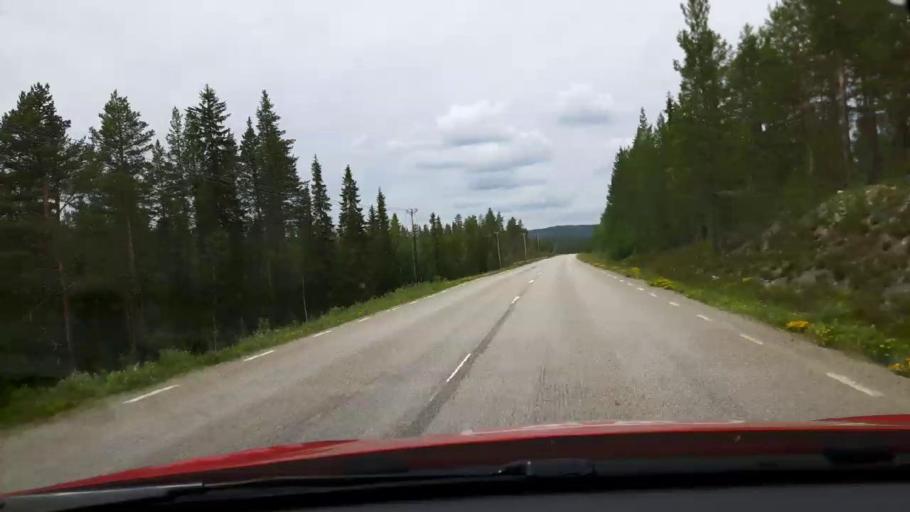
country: SE
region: Jaemtland
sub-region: Harjedalens Kommun
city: Sveg
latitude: 62.3985
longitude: 13.7461
